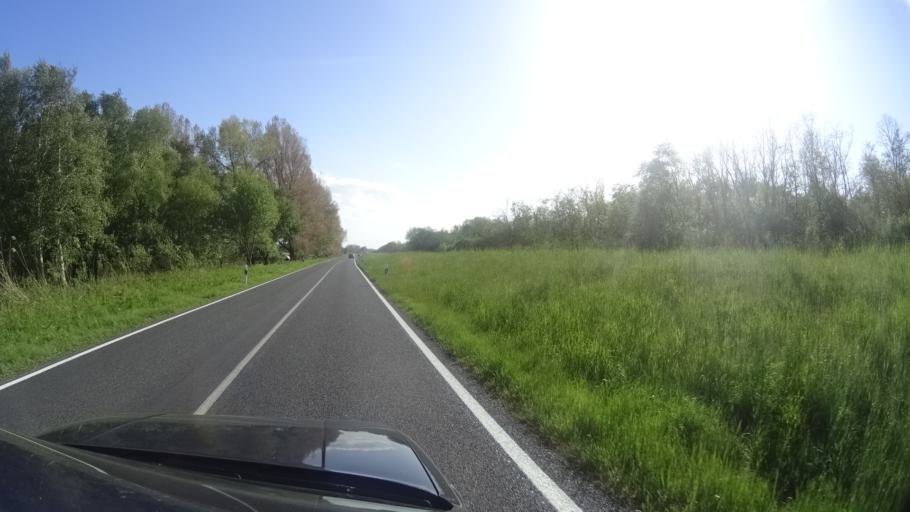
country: DE
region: Mecklenburg-Vorpommern
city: Born
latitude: 54.3975
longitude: 12.4477
